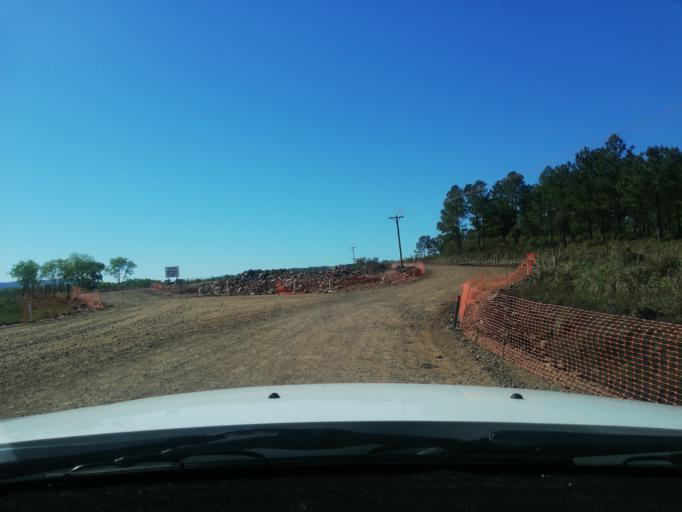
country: AR
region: Misiones
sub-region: Departamento de Candelaria
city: Candelaria
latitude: -27.5302
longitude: -55.7199
